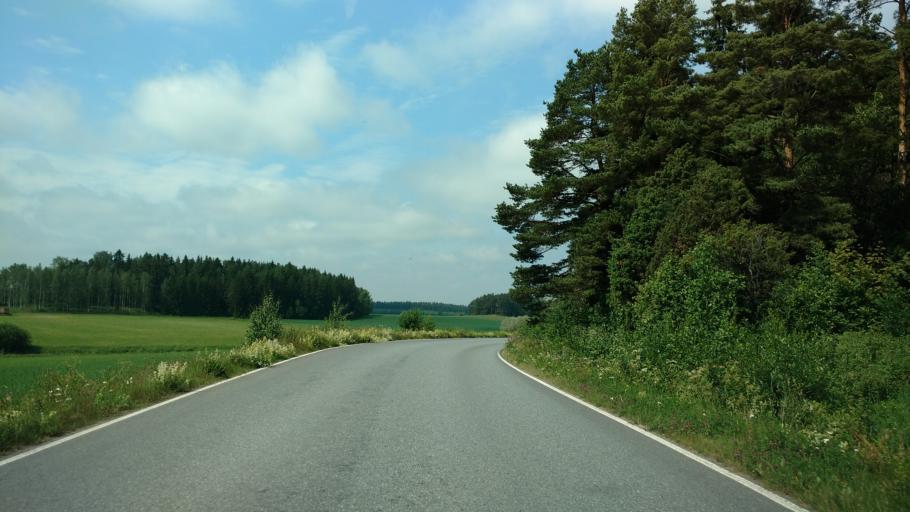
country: FI
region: Haeme
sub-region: Forssa
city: Ypaejae
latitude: 60.7881
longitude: 23.3718
